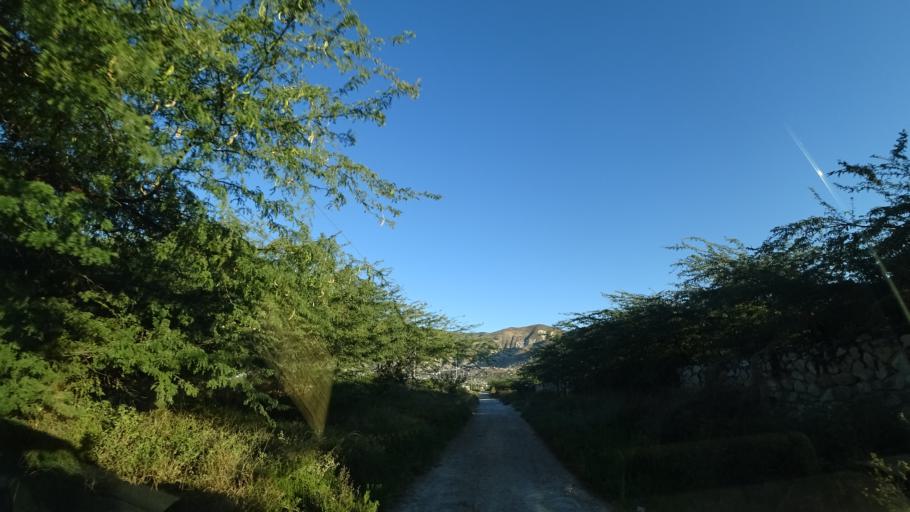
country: HT
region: Ouest
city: Croix des Bouquets
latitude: 18.6536
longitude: -72.2244
